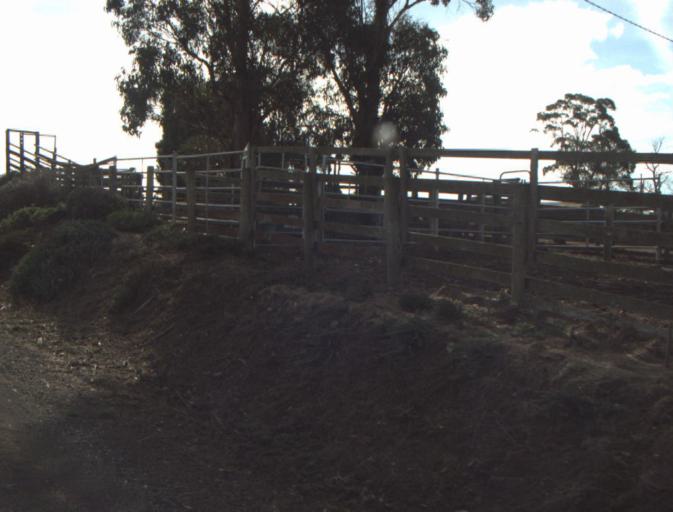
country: AU
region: Tasmania
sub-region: Launceston
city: Mayfield
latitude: -41.2194
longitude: 147.1492
